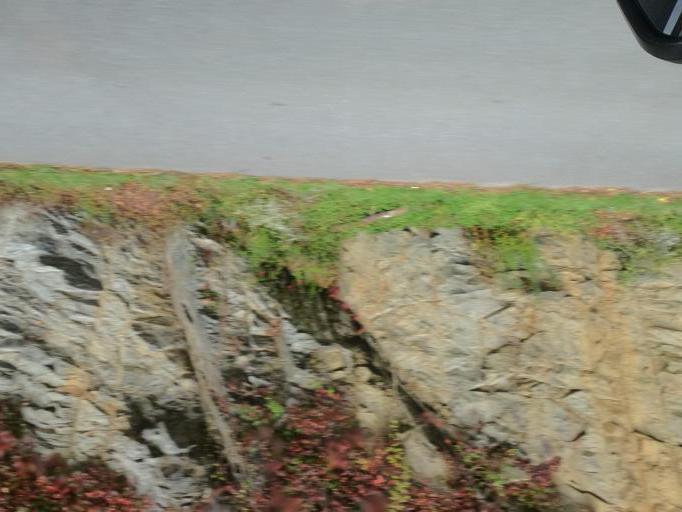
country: US
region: Tennessee
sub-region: Carter County
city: Elizabethton
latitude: 36.2503
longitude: -82.1933
